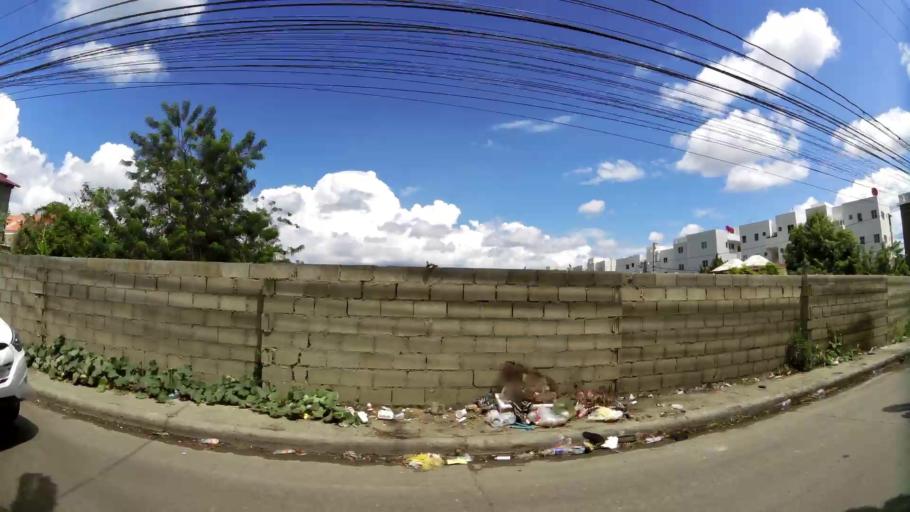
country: DO
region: Santiago
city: Santiago de los Caballeros
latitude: 19.4731
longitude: -70.6666
